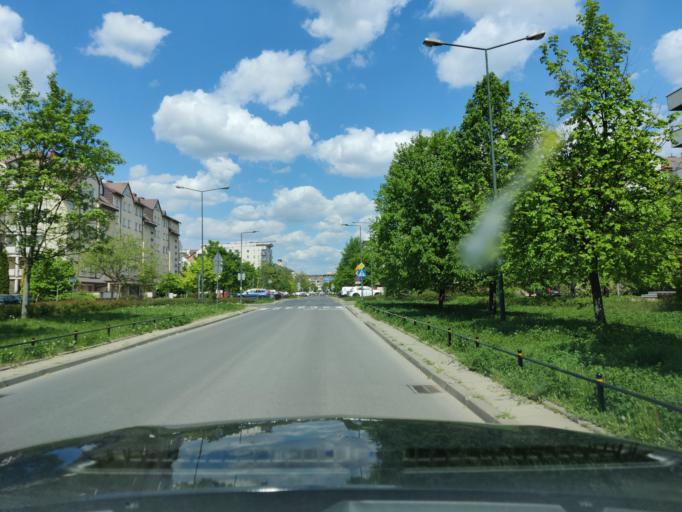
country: PL
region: Masovian Voivodeship
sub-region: Warszawa
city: Kabaty
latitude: 52.1293
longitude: 21.0734
